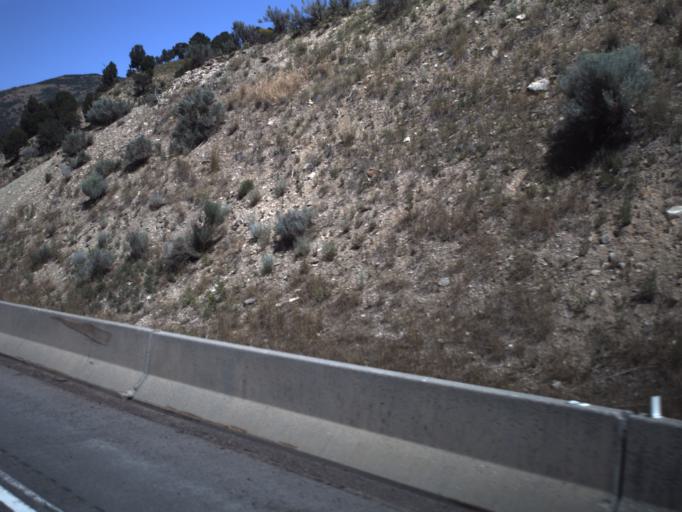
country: US
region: Utah
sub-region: Utah County
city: Mapleton
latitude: 39.9817
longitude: -111.3563
